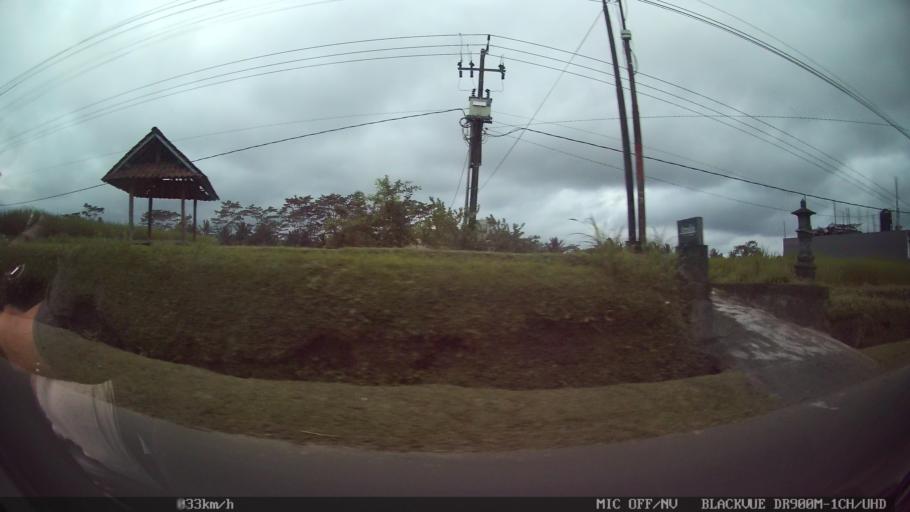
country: ID
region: Bali
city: Bunutan
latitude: -8.4655
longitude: 115.2597
